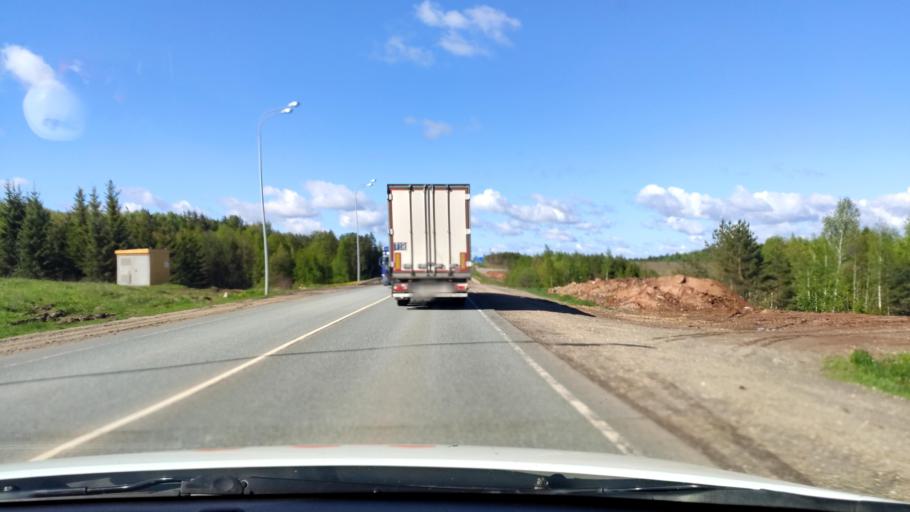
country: RU
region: Tatarstan
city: Sviyazhsk
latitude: 55.7304
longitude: 48.7692
